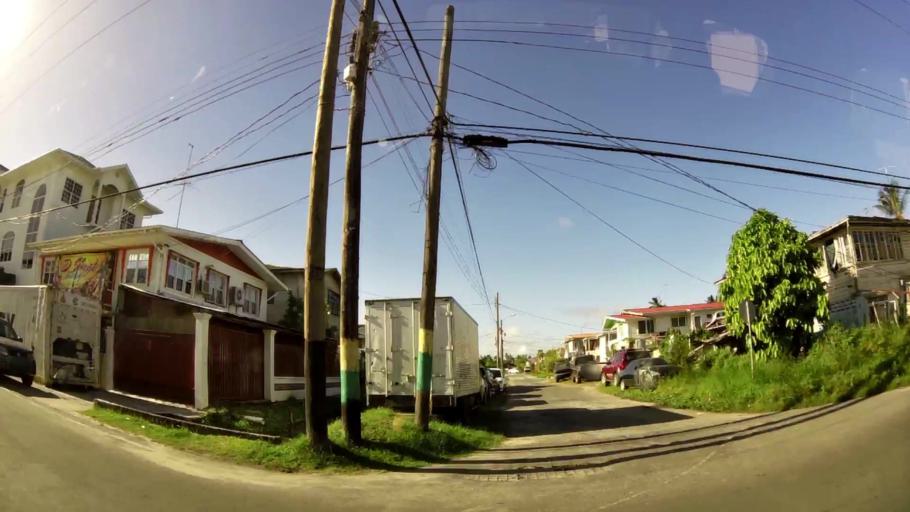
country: GY
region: Demerara-Mahaica
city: Georgetown
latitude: 6.8162
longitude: -58.1375
